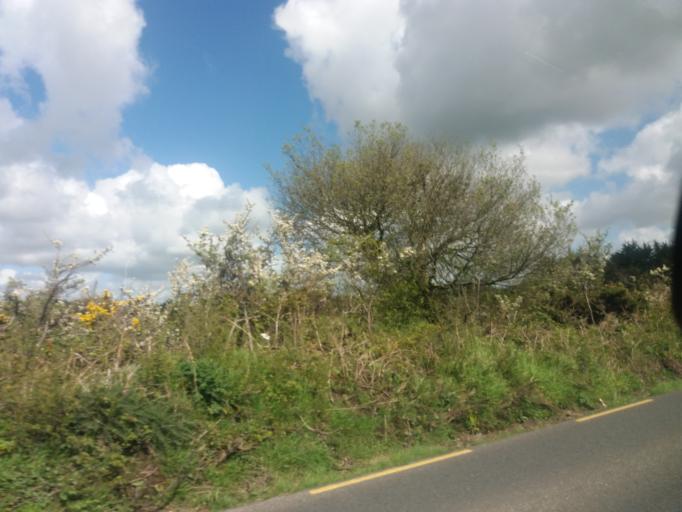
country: IE
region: Leinster
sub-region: Loch Garman
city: Loch Garman
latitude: 52.3189
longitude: -6.5167
